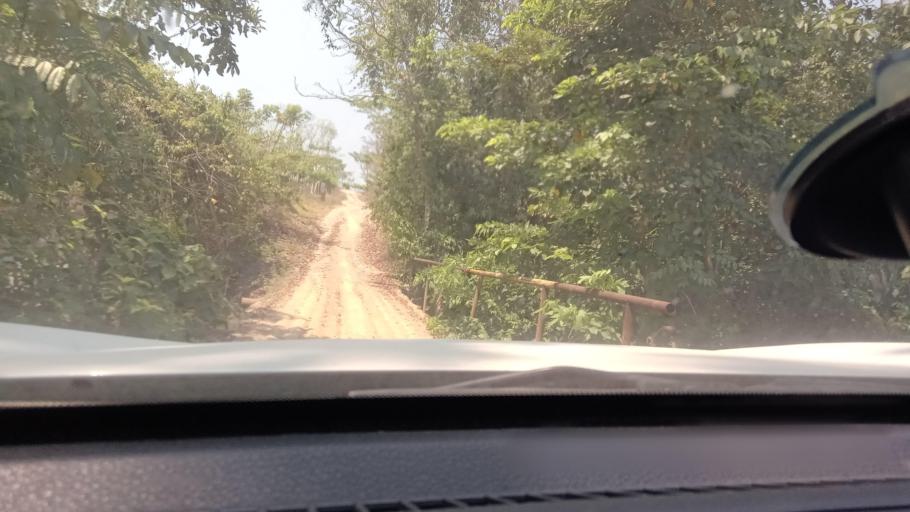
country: MX
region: Tabasco
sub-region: Huimanguillo
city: Francisco Rueda
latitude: 17.4898
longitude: -93.9316
